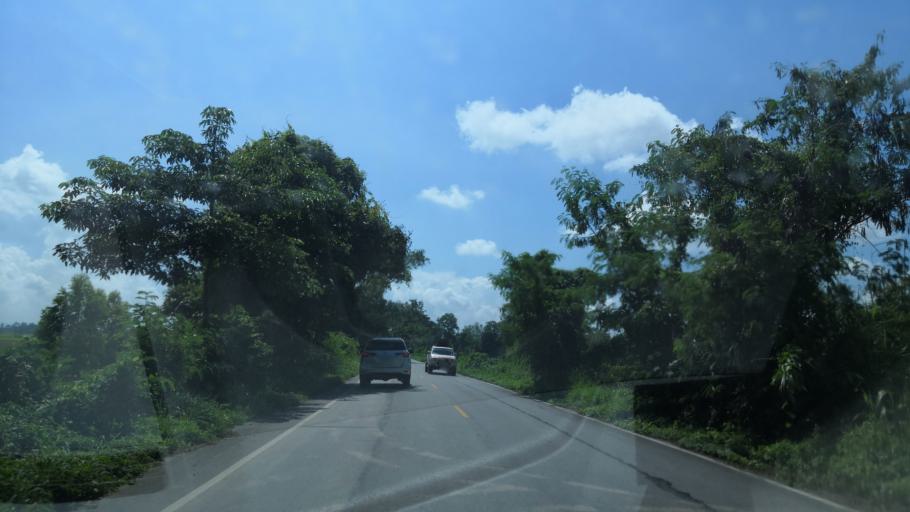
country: TH
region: Chiang Rai
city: Wiang Chai
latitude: 19.9483
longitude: 99.9323
